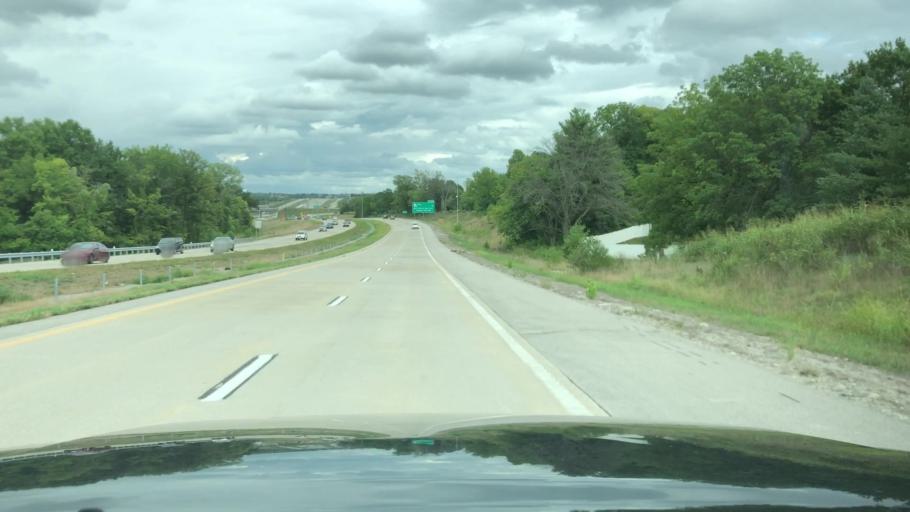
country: US
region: Missouri
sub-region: Saint Charles County
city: Cottleville
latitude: 38.7339
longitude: -90.6473
